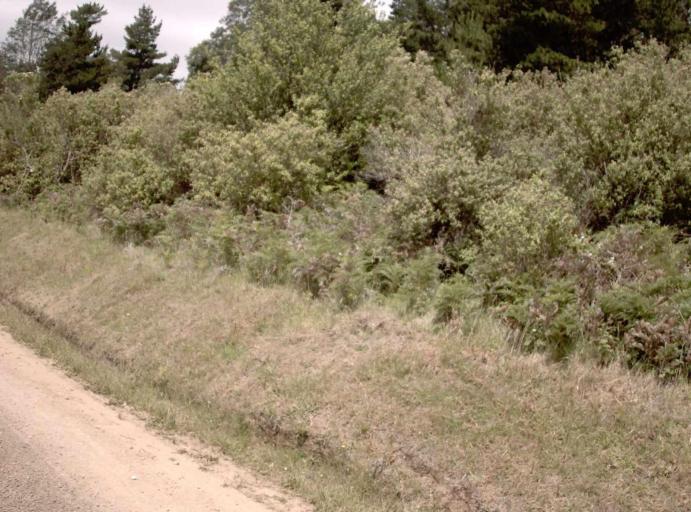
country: AU
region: Victoria
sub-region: Latrobe
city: Traralgon
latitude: -38.4165
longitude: 146.6130
